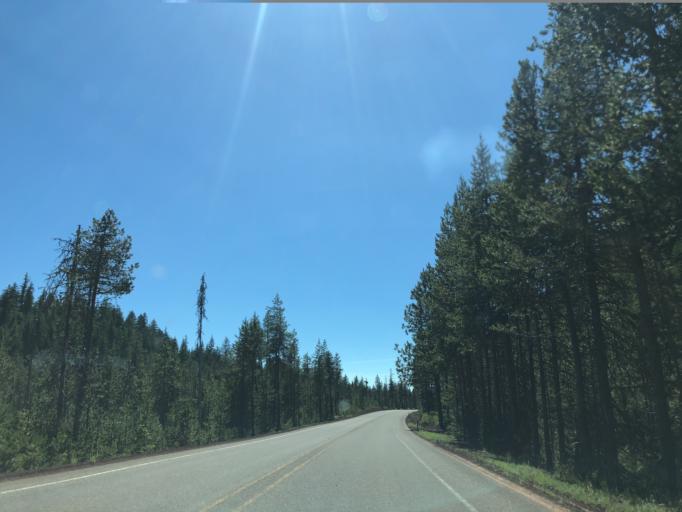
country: US
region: Oregon
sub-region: Deschutes County
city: Sisters
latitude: 44.4341
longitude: -121.9515
